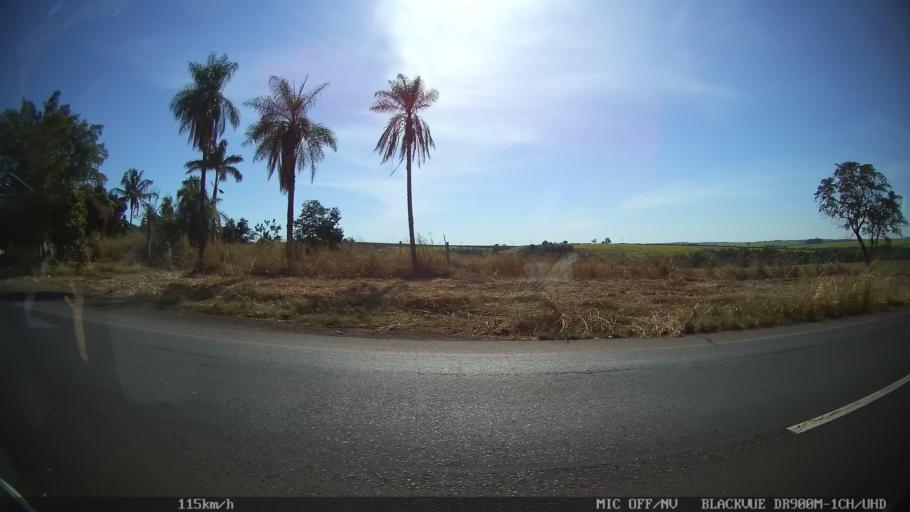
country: BR
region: Sao Paulo
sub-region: Barretos
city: Barretos
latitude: -20.5937
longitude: -48.7137
